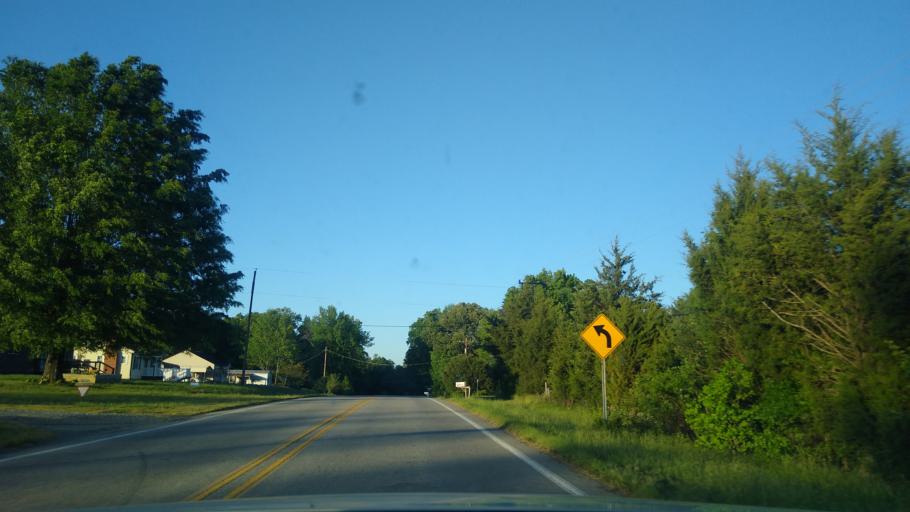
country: US
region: North Carolina
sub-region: Rockingham County
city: Reidsville
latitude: 36.3732
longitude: -79.5958
